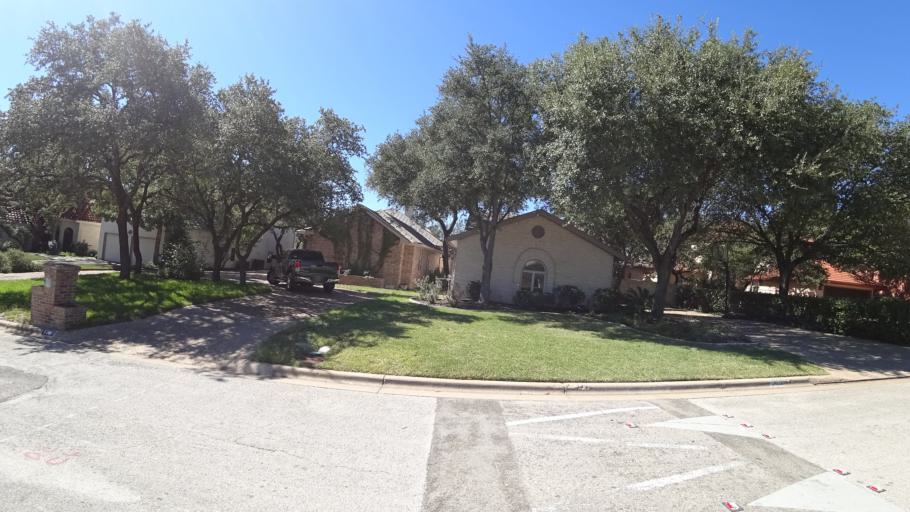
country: US
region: Texas
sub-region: Travis County
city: West Lake Hills
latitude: 30.3355
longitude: -97.7792
